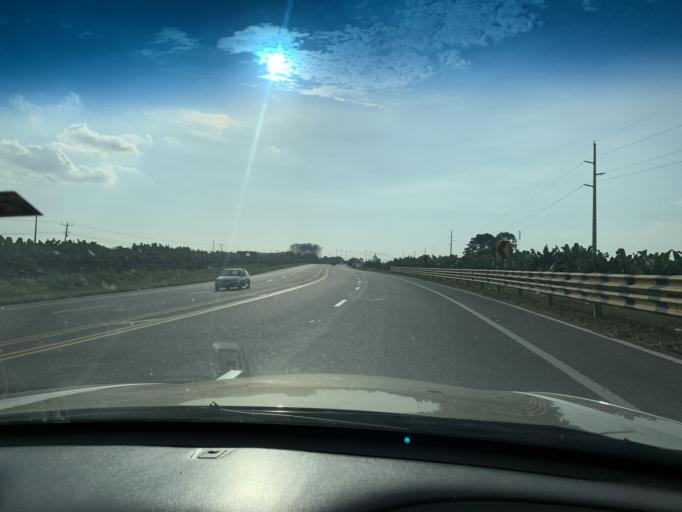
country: EC
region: Guayas
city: Naranjito
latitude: -2.2588
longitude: -79.5527
